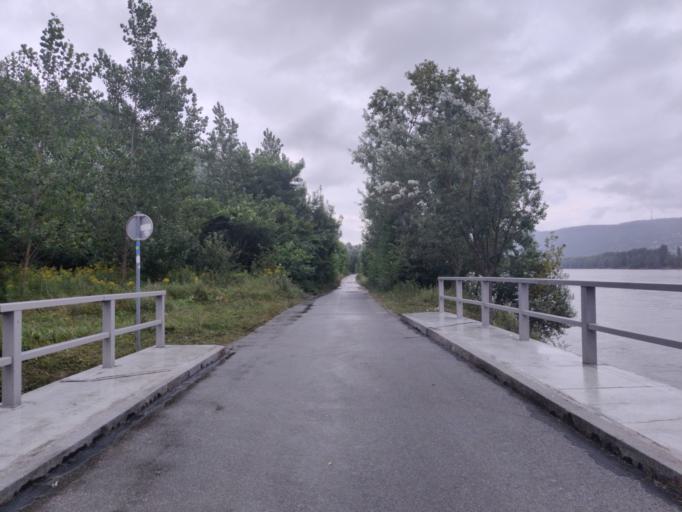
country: AT
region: Lower Austria
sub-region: Politischer Bezirk Korneuburg
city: Langenzersdorf
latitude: 48.3160
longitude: 16.3420
